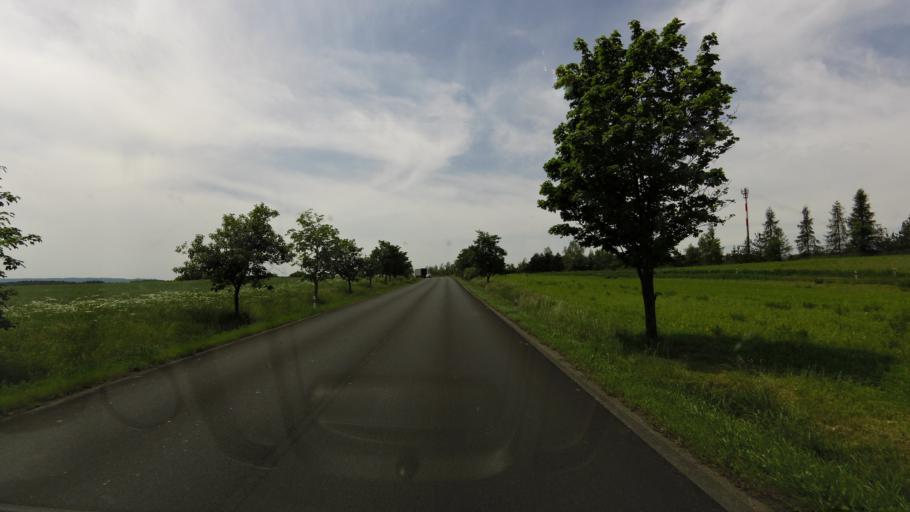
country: CZ
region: Plzensky
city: Zbiroh
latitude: 49.8209
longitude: 13.7718
